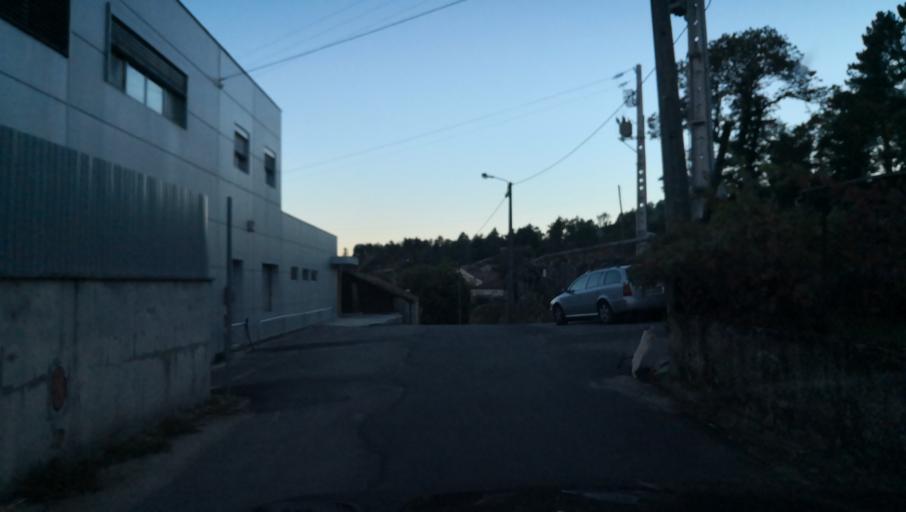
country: PT
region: Vila Real
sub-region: Santa Marta de Penaguiao
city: Santa Marta de Penaguiao
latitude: 41.2728
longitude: -7.8102
